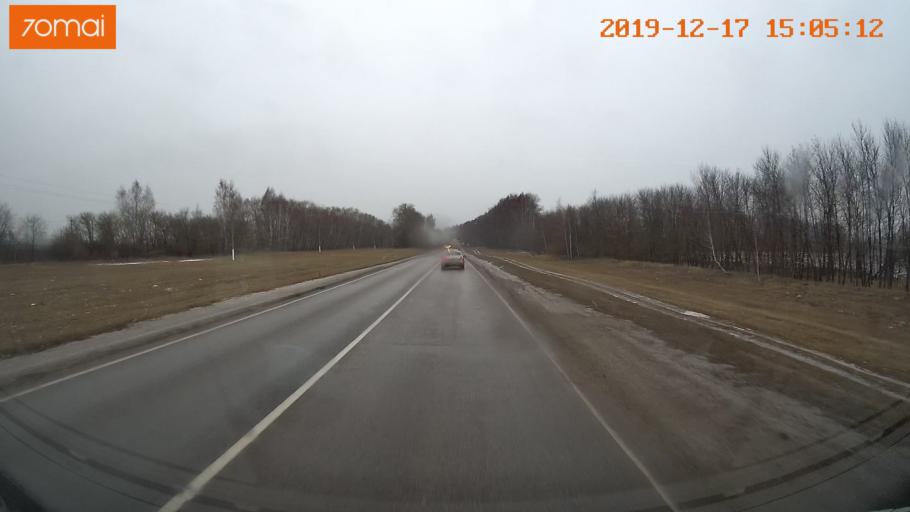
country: RU
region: Rjazan
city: Mikhaylov
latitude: 54.2657
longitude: 39.1196
